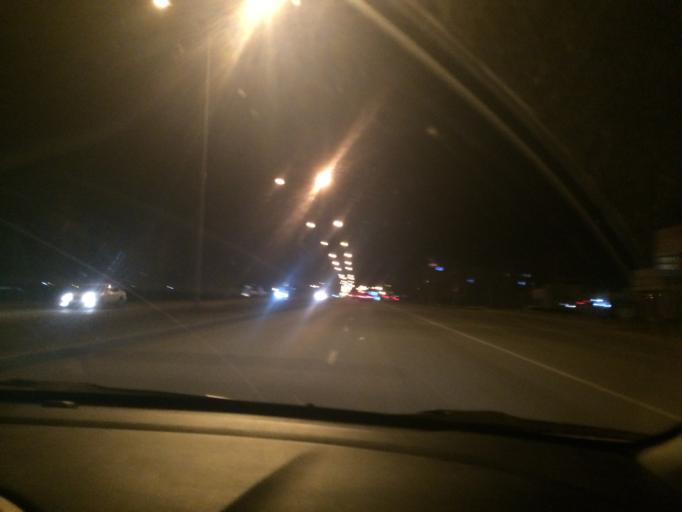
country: KZ
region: Astana Qalasy
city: Astana
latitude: 51.1959
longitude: 71.4711
